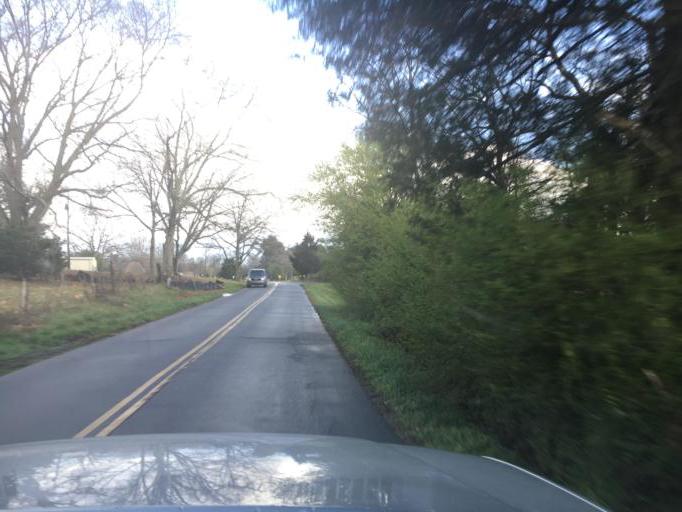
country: US
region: South Carolina
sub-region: Greenville County
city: Parker
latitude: 34.8634
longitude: -82.5063
